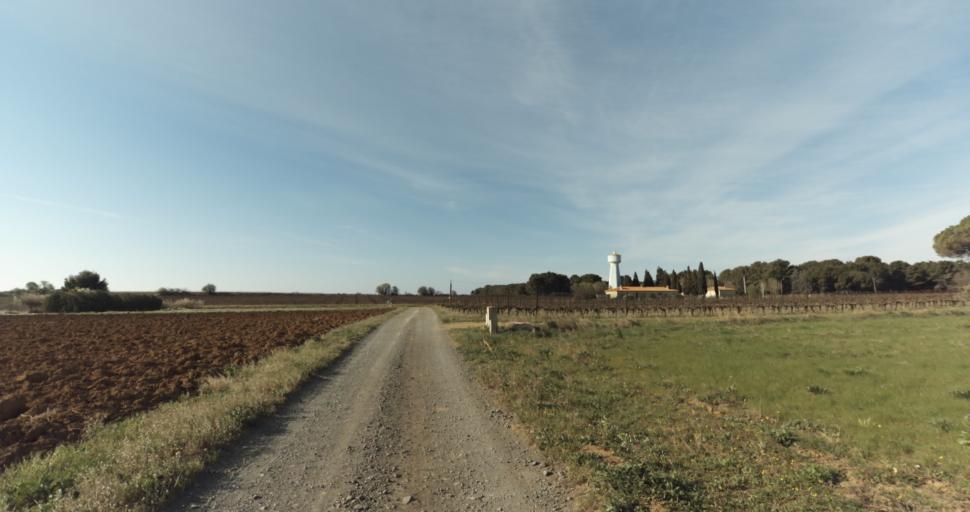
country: FR
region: Languedoc-Roussillon
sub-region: Departement de l'Herault
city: Pomerols
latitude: 43.3697
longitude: 3.5034
